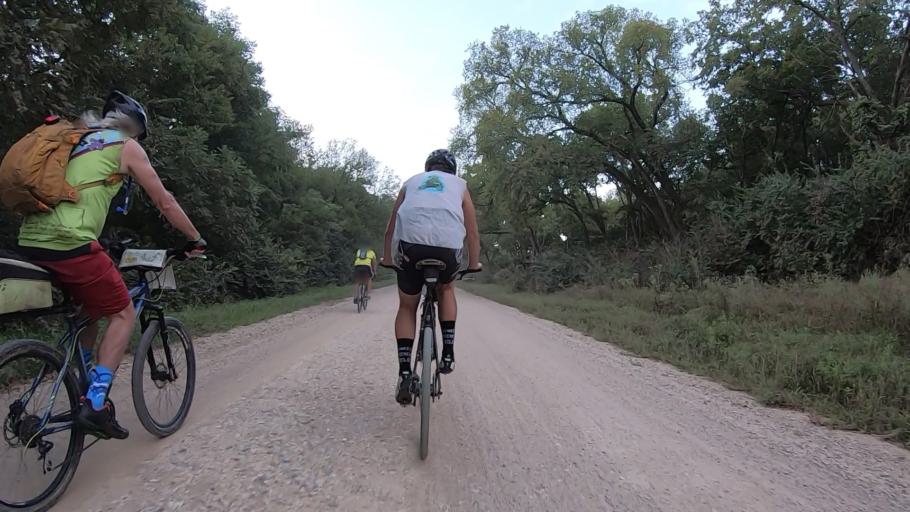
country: US
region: Kansas
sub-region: Marshall County
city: Marysville
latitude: 39.8325
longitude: -96.6650
